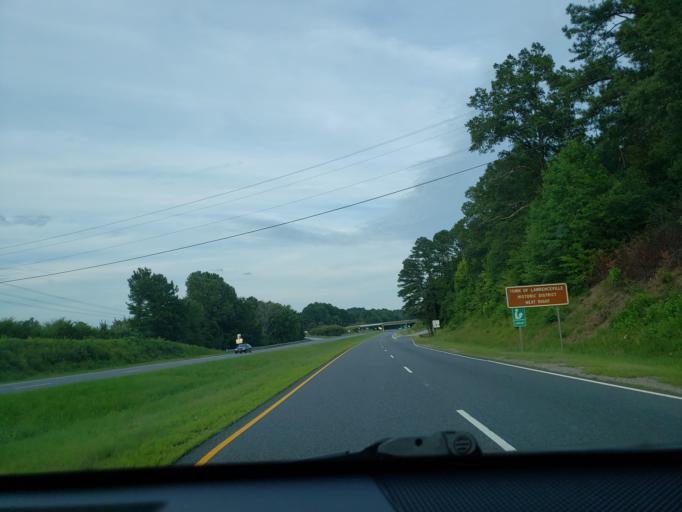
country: US
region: Virginia
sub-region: Brunswick County
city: Lawrenceville
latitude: 36.7481
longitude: -77.8597
